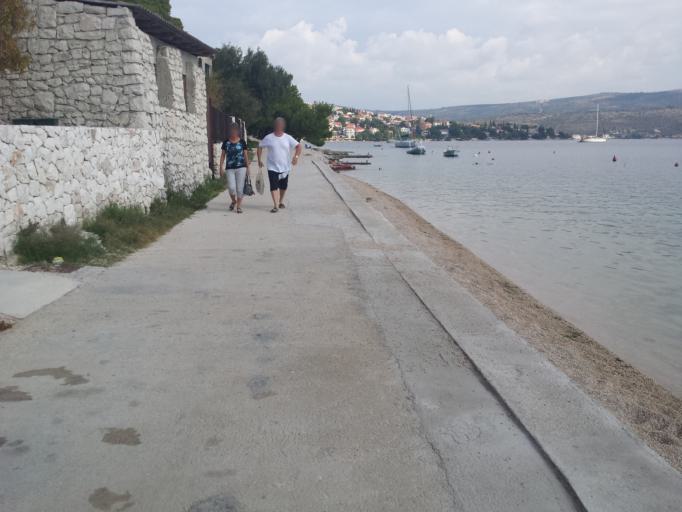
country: HR
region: Sibensko-Kniniska
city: Rogoznica
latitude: 43.5261
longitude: 15.9727
